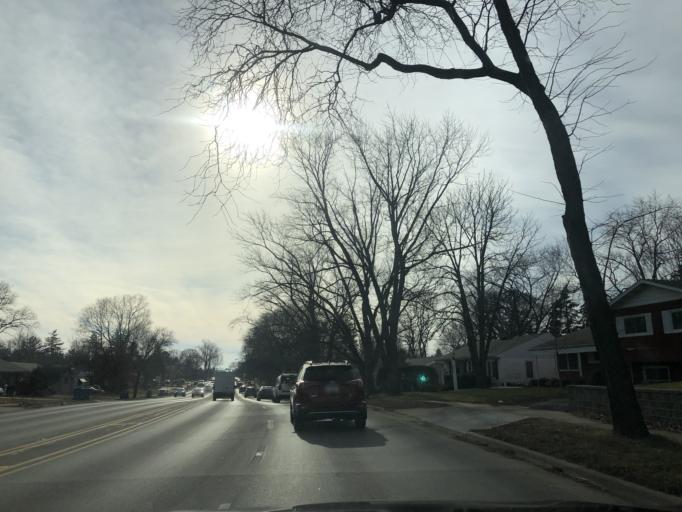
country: US
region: Illinois
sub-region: DuPage County
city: Downers Grove
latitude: 41.8150
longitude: -88.0114
